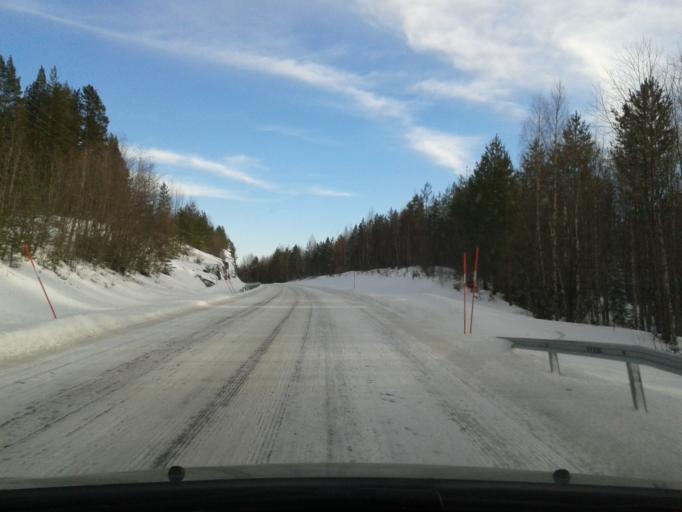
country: SE
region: Vaesterbotten
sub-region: Asele Kommun
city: Asele
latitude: 64.3238
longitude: 17.0720
